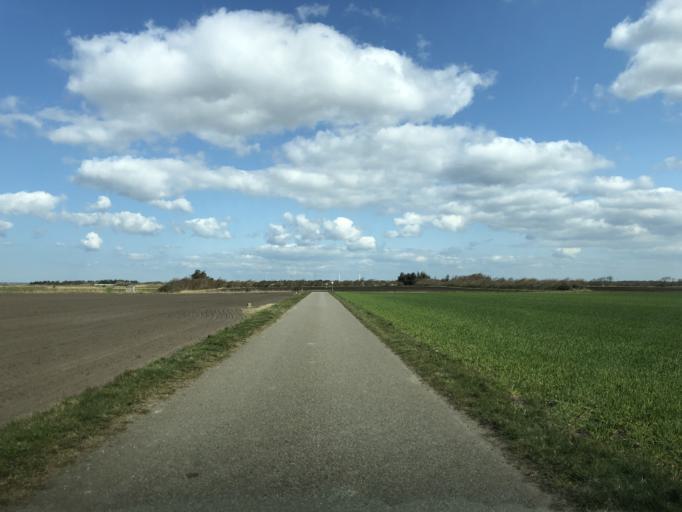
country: DK
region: Central Jutland
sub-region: Holstebro Kommune
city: Ulfborg
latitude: 56.4017
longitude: 8.1768
